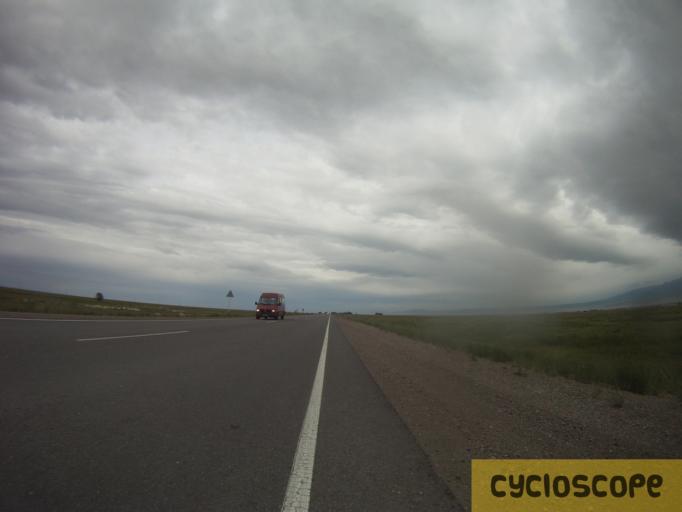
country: KZ
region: Zhambyl
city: Georgiyevka
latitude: 43.3788
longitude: 75.0496
